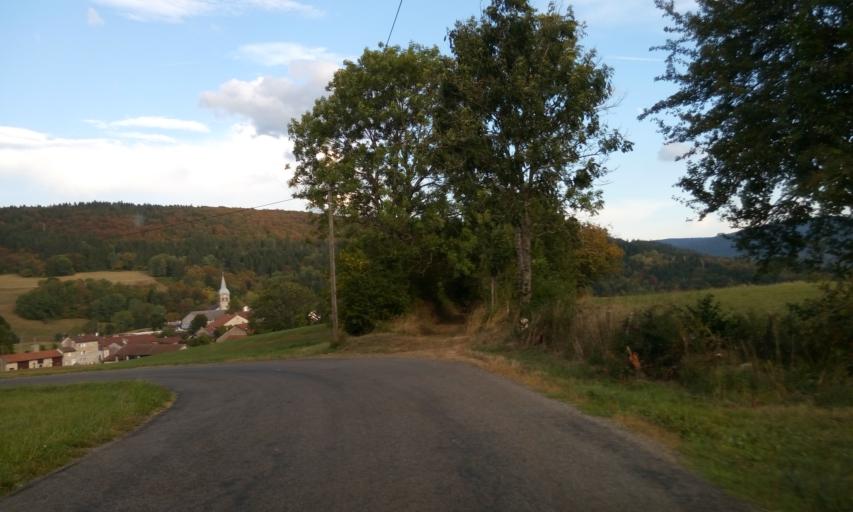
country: FR
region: Rhone-Alpes
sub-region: Departement de l'Ain
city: Nantua
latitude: 46.1844
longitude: 5.6803
